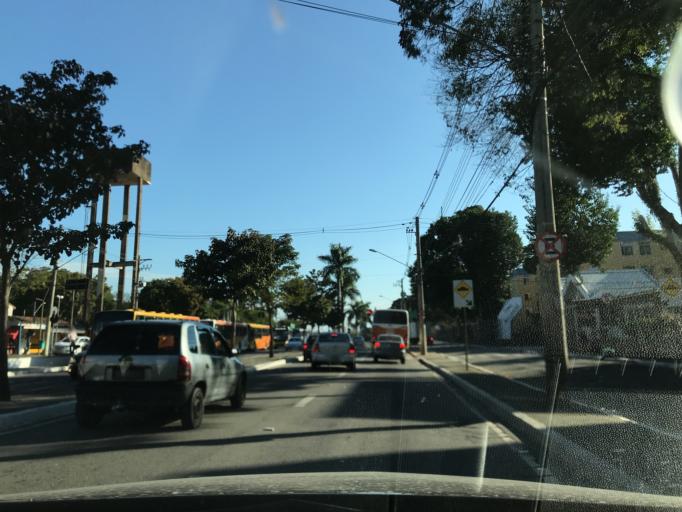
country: BR
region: Sao Paulo
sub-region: Sao Jose Dos Campos
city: Sao Jose dos Campos
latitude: -23.1841
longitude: -45.8602
